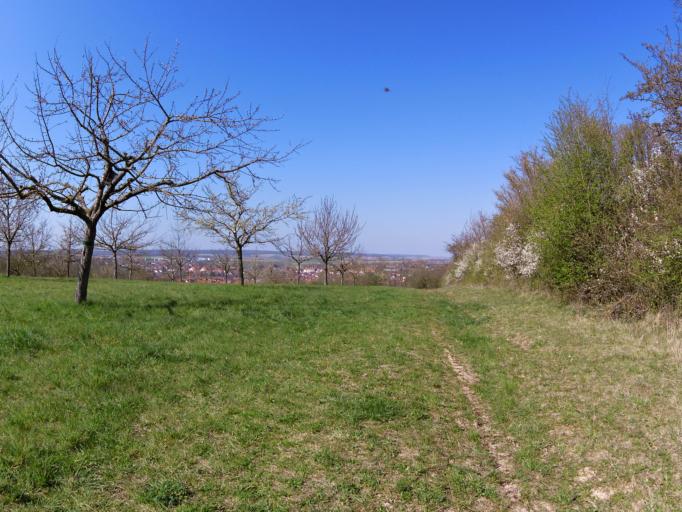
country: DE
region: Bavaria
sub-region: Regierungsbezirk Unterfranken
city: Kurnach
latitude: 49.8380
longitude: 10.0487
